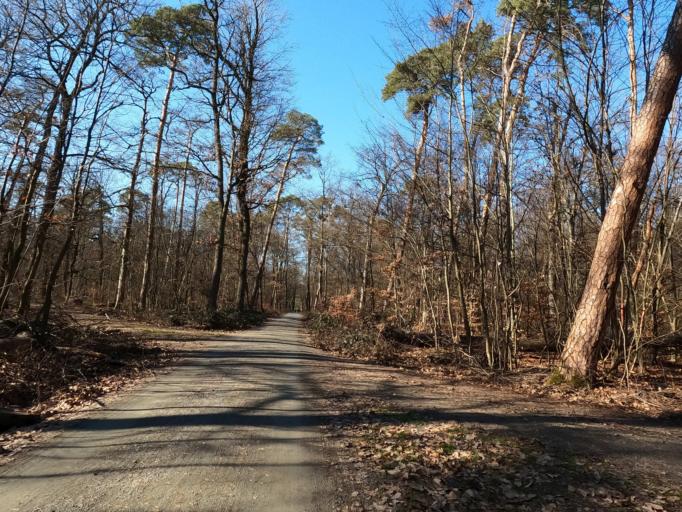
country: DE
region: Hesse
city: Kelsterbach
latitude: 50.0643
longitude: 8.5753
